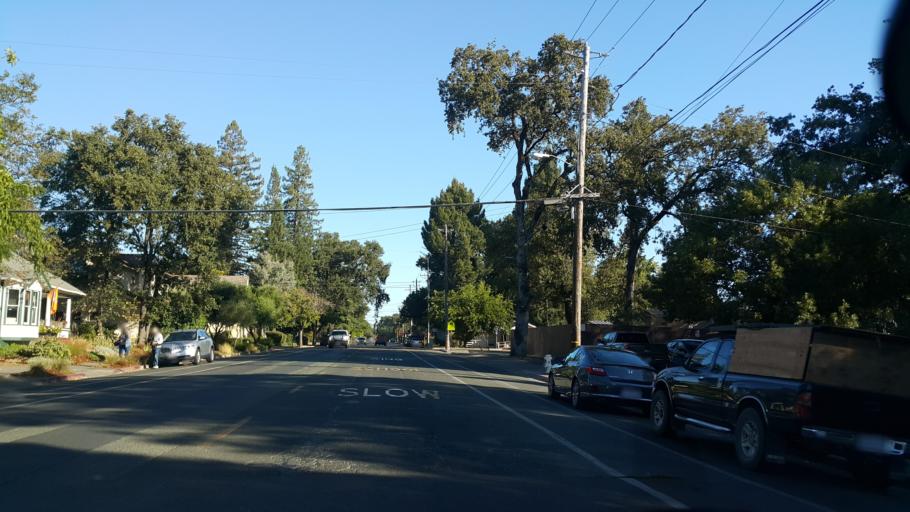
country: US
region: California
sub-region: Mendocino County
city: Ukiah
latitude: 39.1458
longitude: -123.2115
